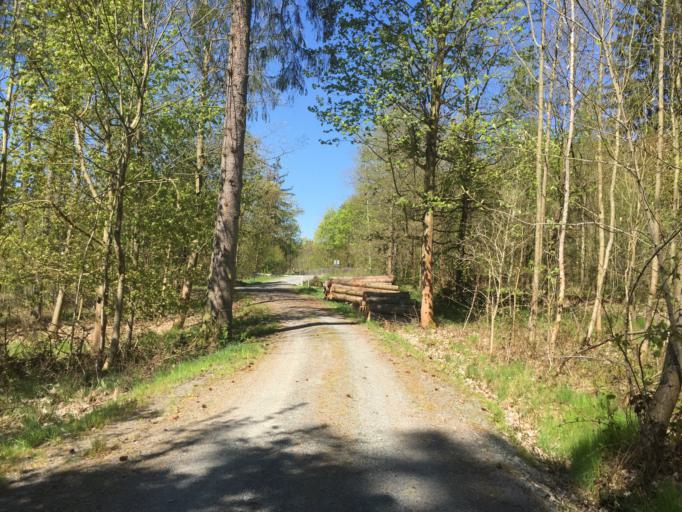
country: DE
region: Saxony
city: Neuensalz
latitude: 50.5037
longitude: 12.1937
